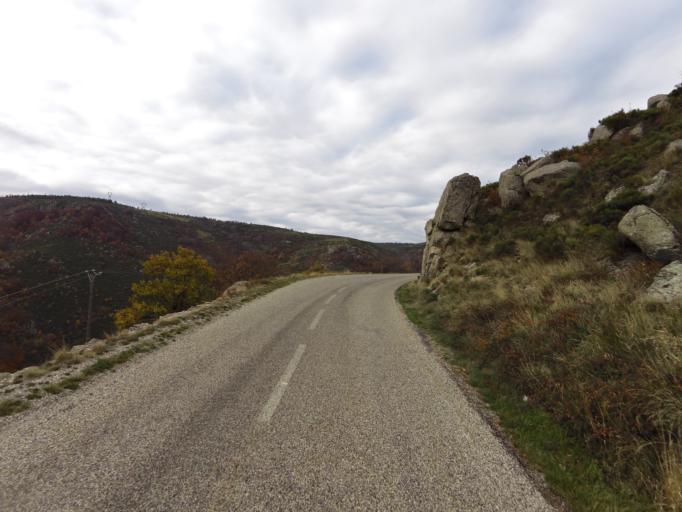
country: FR
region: Rhone-Alpes
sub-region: Departement de l'Ardeche
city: Les Vans
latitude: 44.5177
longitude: 4.0258
